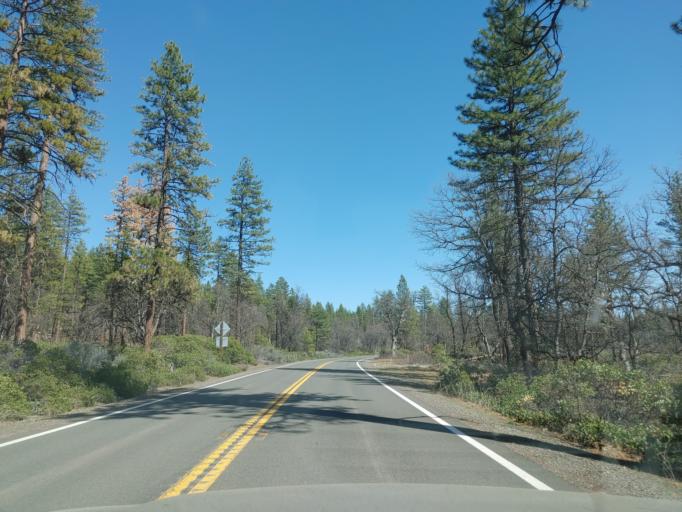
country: US
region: California
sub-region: Shasta County
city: Burney
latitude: 41.0081
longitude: -121.6390
